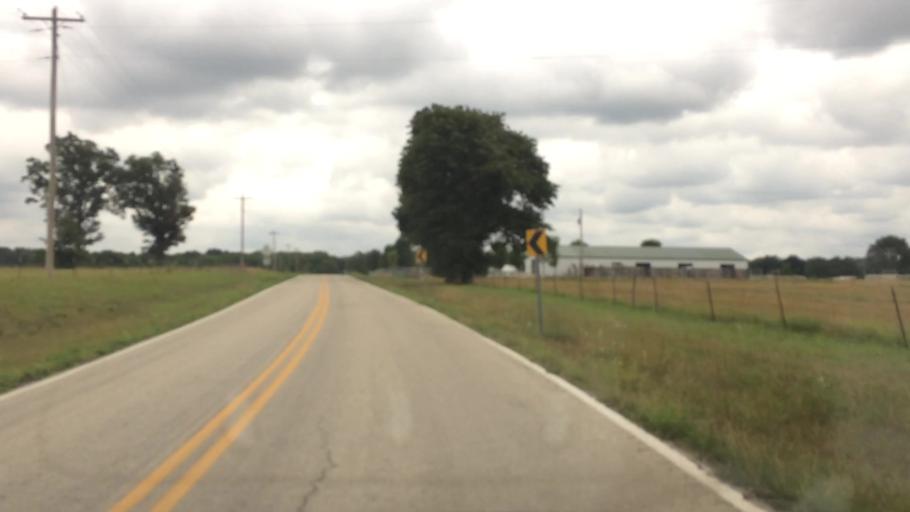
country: US
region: Missouri
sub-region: Greene County
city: Strafford
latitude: 37.2960
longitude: -93.1188
